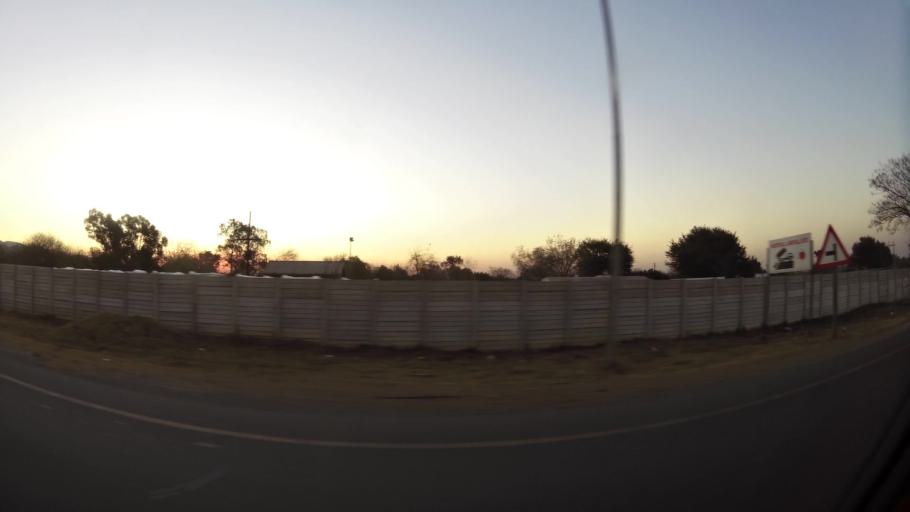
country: ZA
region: North-West
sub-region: Bojanala Platinum District Municipality
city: Rustenburg
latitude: -25.6488
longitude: 27.2532
